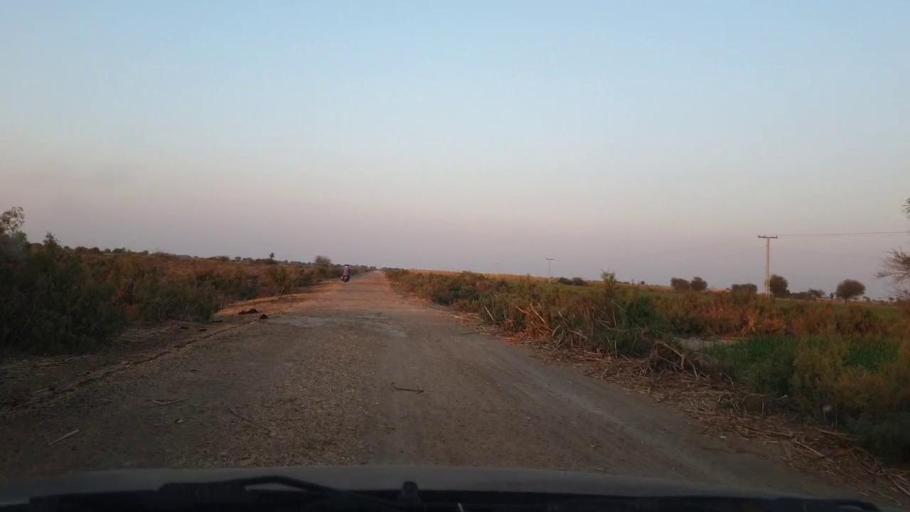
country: PK
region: Sindh
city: Jhol
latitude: 25.9231
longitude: 68.9642
